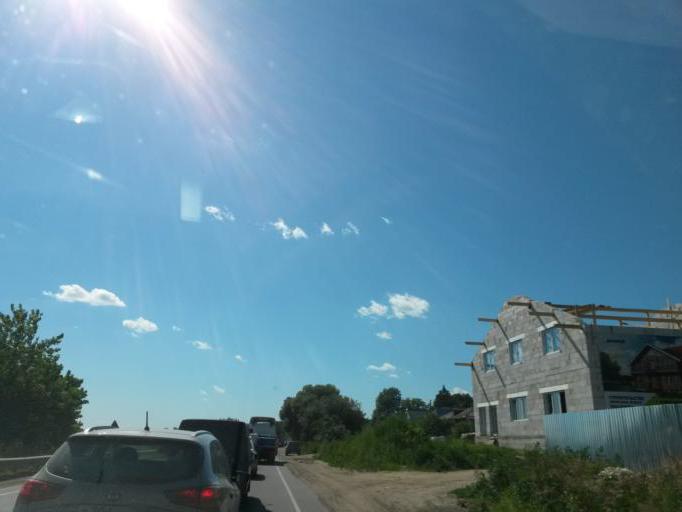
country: RU
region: Moskovskaya
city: Serpukhov
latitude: 54.8934
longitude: 37.3204
